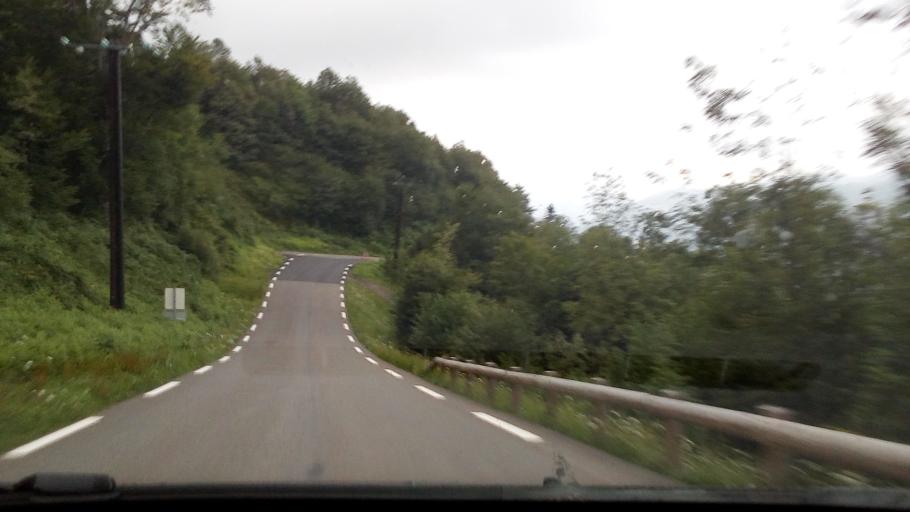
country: FR
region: Midi-Pyrenees
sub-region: Departement des Hautes-Pyrenees
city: Argeles-Gazost
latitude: 42.9652
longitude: -0.2232
